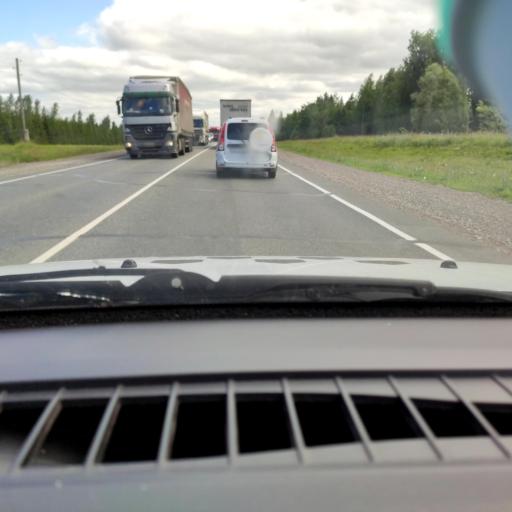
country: RU
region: Udmurtiya
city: Pychas
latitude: 56.4829
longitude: 52.5510
